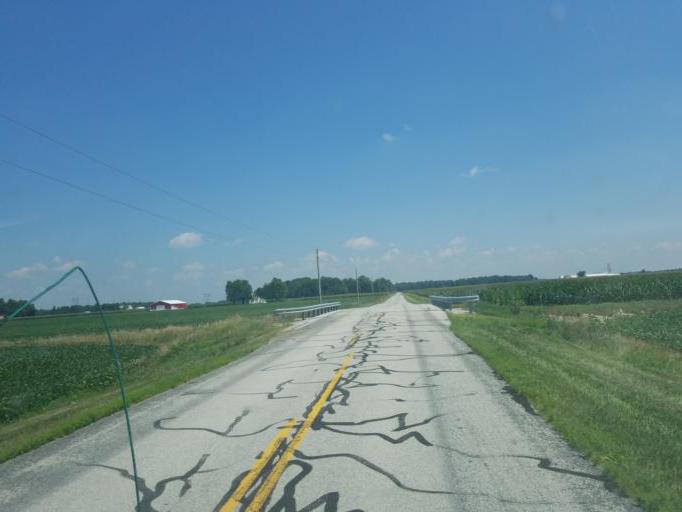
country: US
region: Ohio
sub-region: Auglaize County
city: Wapakoneta
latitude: 40.5404
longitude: -84.2493
